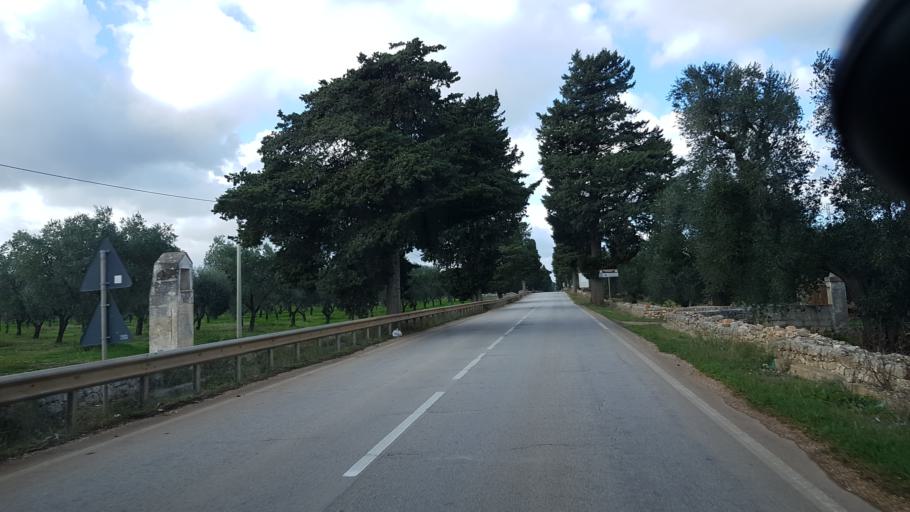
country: IT
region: Apulia
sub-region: Provincia di Brindisi
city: Montalbano
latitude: 40.7638
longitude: 17.5217
